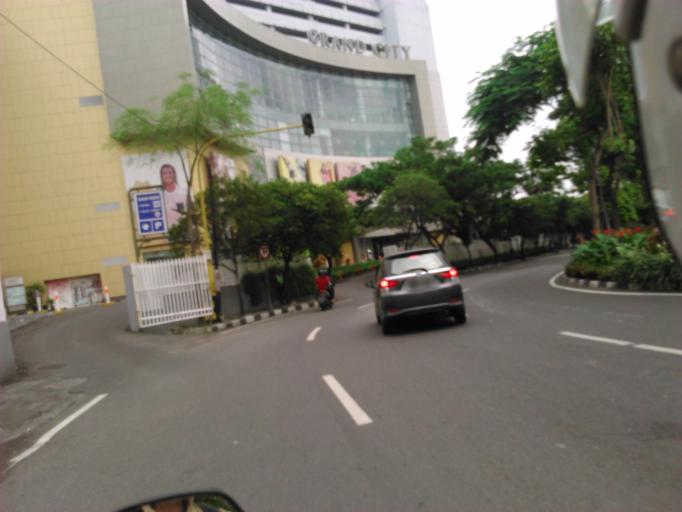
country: ID
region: East Java
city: Pacarkeling
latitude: -7.2622
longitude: 112.7515
